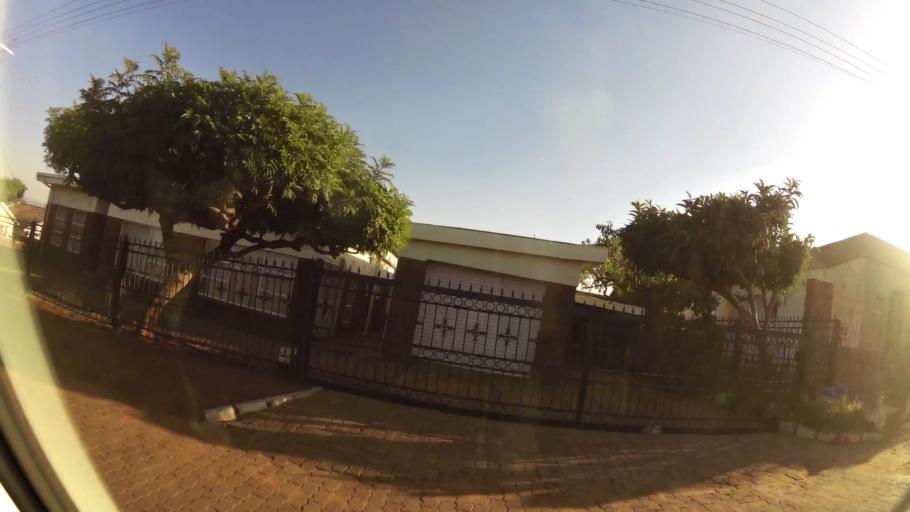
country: ZA
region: Gauteng
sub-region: City of Tshwane Metropolitan Municipality
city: Cullinan
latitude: -25.7019
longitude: 28.3888
